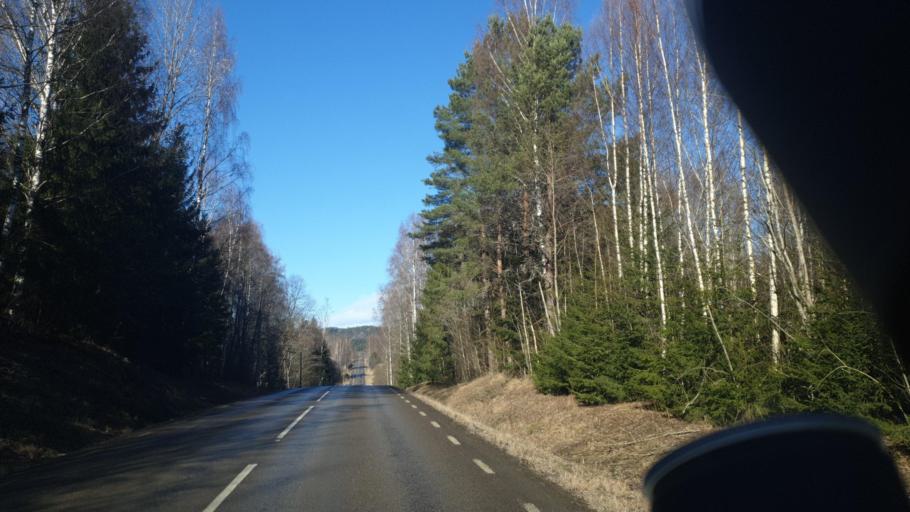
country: SE
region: Vaermland
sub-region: Eda Kommun
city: Amotfors
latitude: 59.6646
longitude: 12.4251
